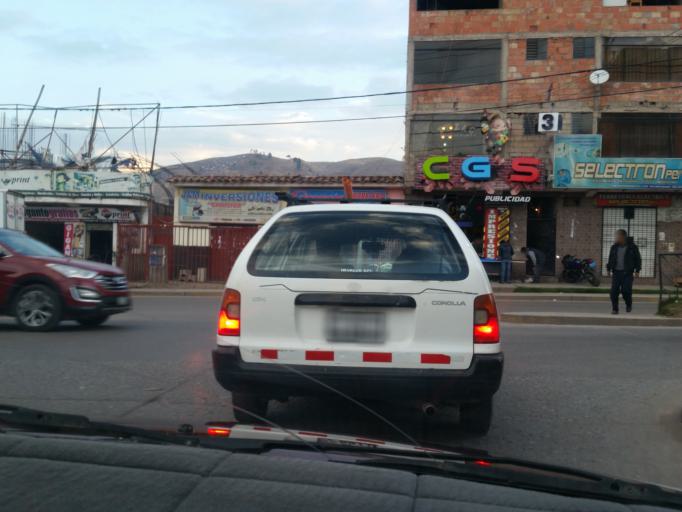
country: PE
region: Cusco
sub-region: Provincia de Cusco
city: Cusco
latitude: -13.5261
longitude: -71.9615
